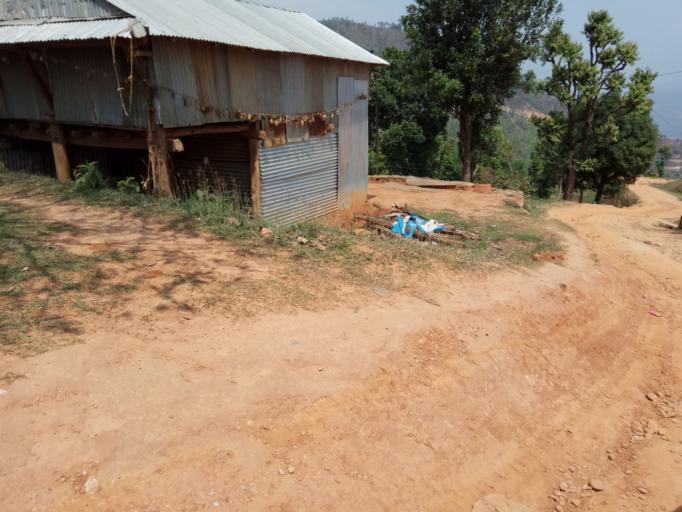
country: NP
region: Central Region
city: Kirtipur
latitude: 27.8924
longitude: 85.0809
